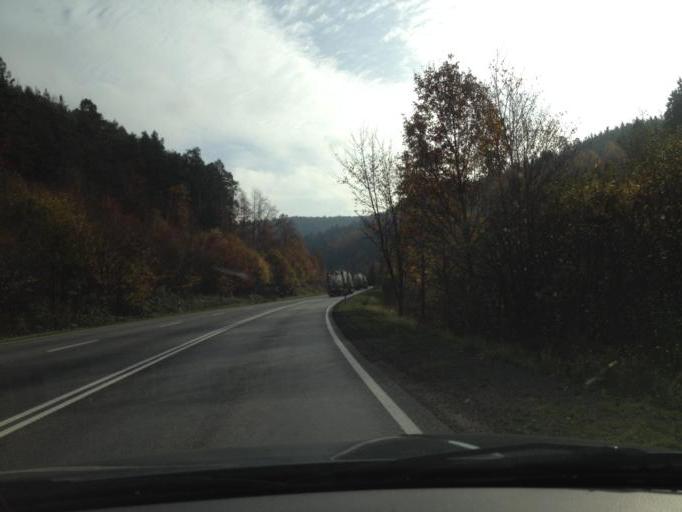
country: DE
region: Rheinland-Pfalz
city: Erfweiler
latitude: 49.2047
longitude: 7.8086
